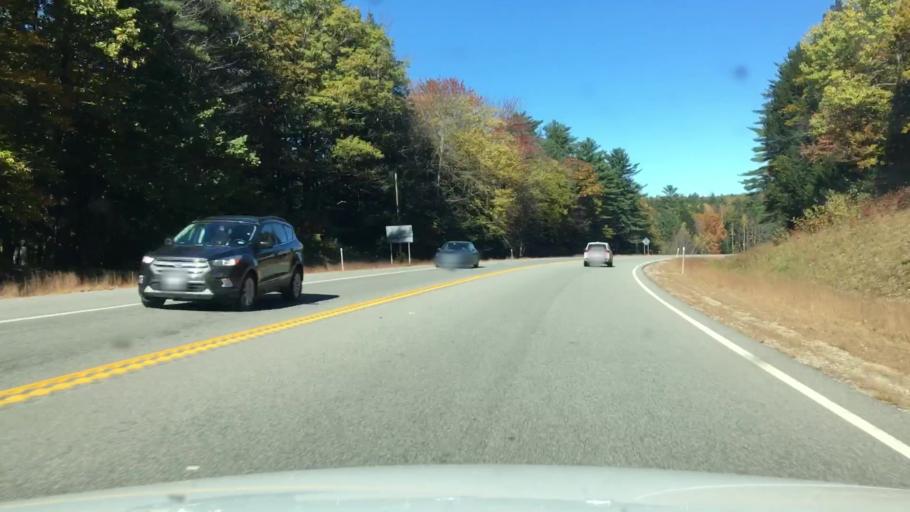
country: US
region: New Hampshire
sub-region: Carroll County
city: Sanbornville
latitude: 43.5000
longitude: -71.0285
